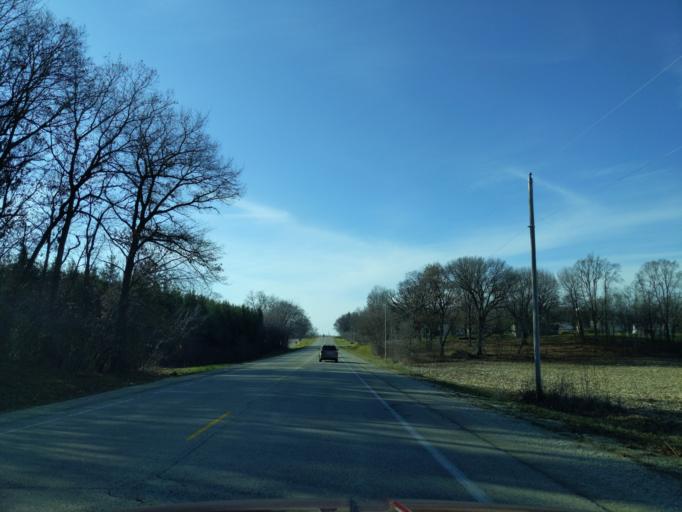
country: US
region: Wisconsin
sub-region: Rock County
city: Milton
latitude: 42.8255
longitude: -88.8931
